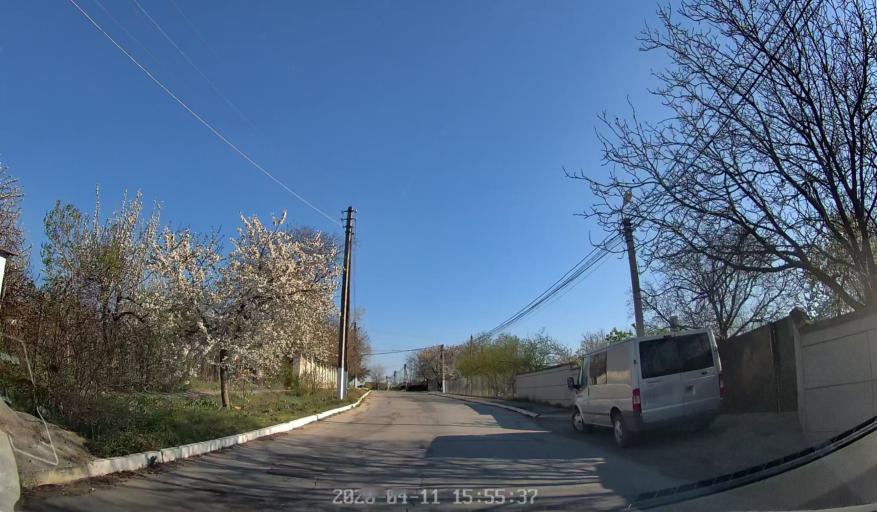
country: MD
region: Chisinau
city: Vadul lui Voda
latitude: 47.0952
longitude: 29.1773
